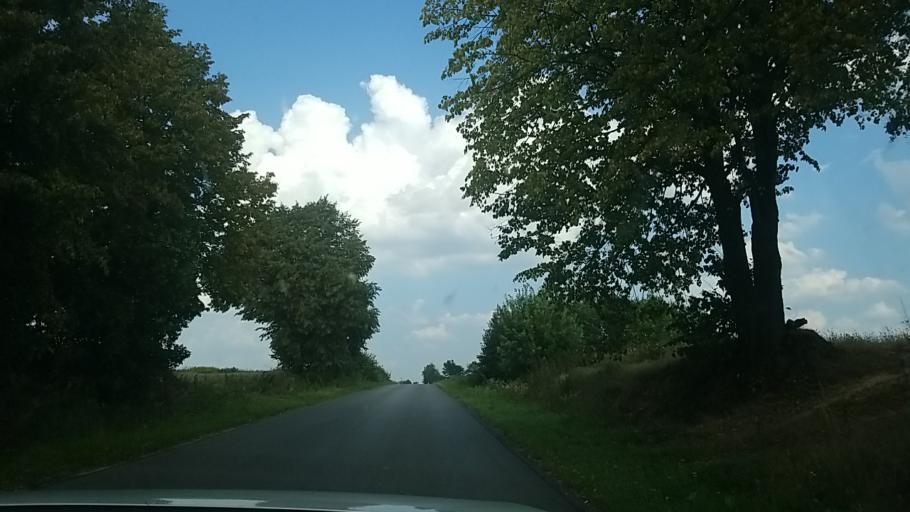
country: PL
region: Lublin Voivodeship
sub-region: Powiat janowski
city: Dzwola
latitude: 50.7106
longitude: 22.5830
